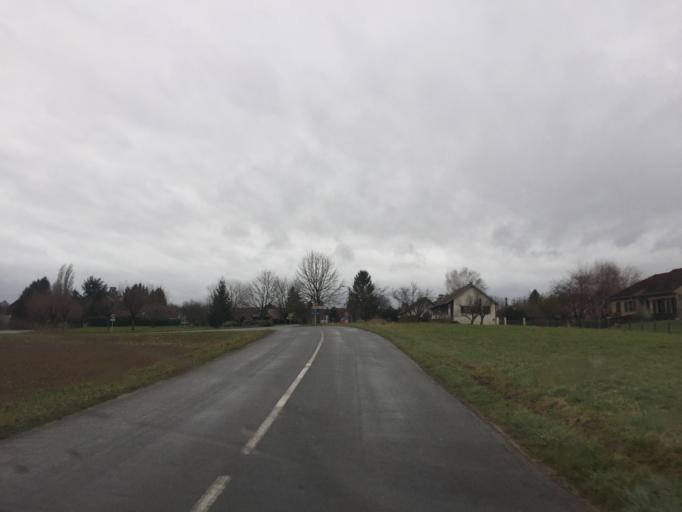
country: FR
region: Franche-Comte
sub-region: Departement du Jura
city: Dole
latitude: 47.1468
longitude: 5.5578
